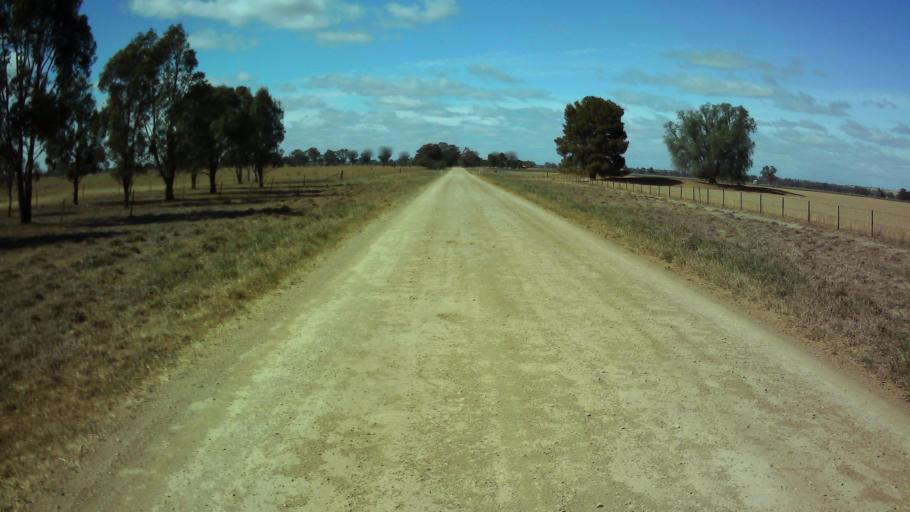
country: AU
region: New South Wales
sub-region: Weddin
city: Grenfell
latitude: -34.0217
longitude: 148.3191
